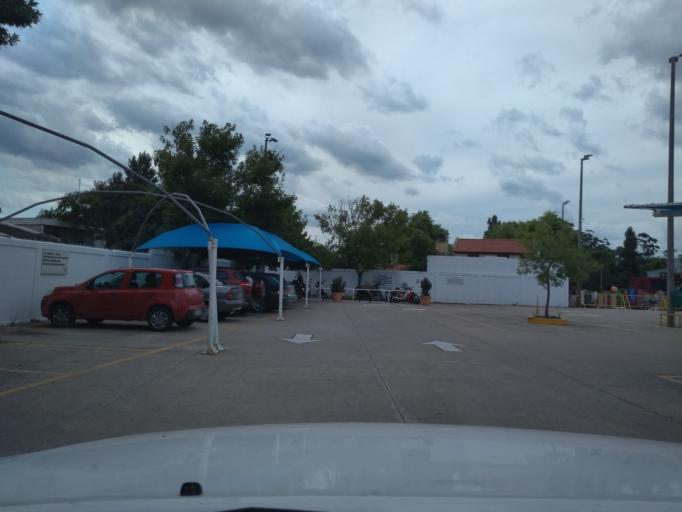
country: UY
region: Canelones
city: Barra de Carrasco
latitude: -34.8702
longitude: -56.0225
